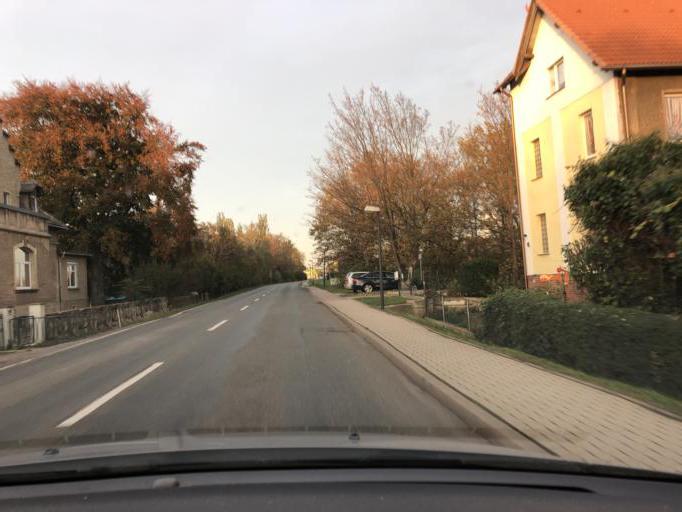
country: DE
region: Saxony
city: Elstertrebnitz
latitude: 51.1057
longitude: 12.1865
